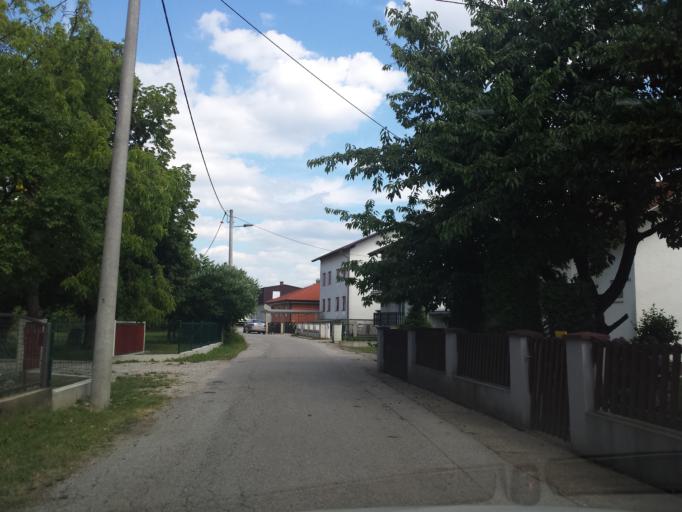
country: HR
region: Grad Zagreb
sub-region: Sesvete
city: Sesvete
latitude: 45.8227
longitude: 16.1546
